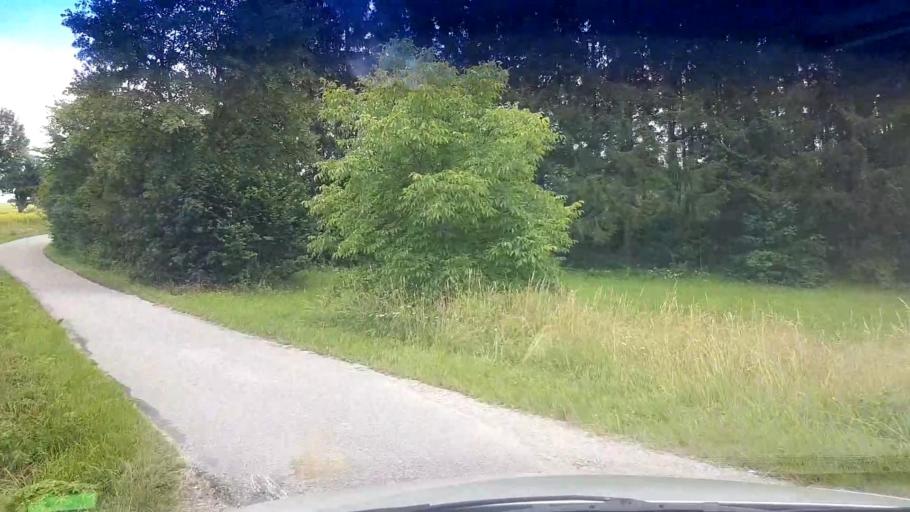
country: DE
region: Bavaria
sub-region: Upper Franconia
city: Poxdorf
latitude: 49.8937
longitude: 11.0801
